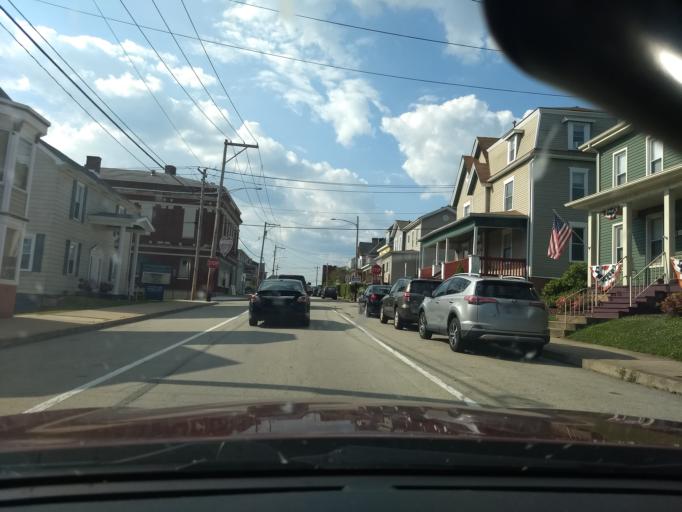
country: US
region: Pennsylvania
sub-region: Westmoreland County
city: Irwin
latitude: 40.3294
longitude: -79.7094
